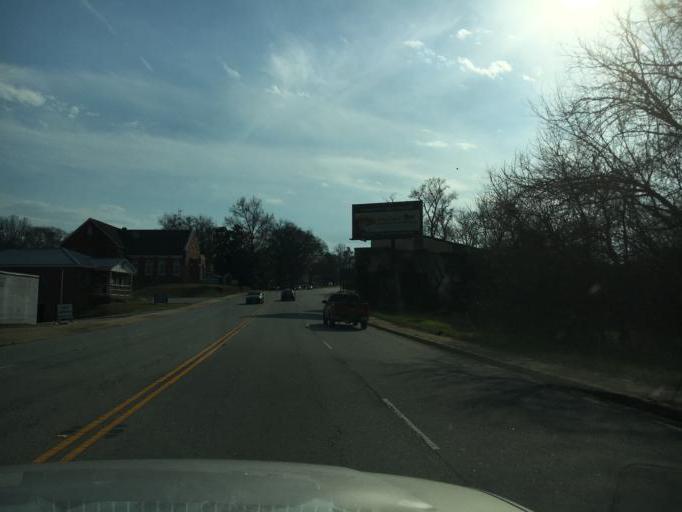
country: US
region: South Carolina
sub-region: Spartanburg County
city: Spartanburg
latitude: 34.9827
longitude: -81.9291
